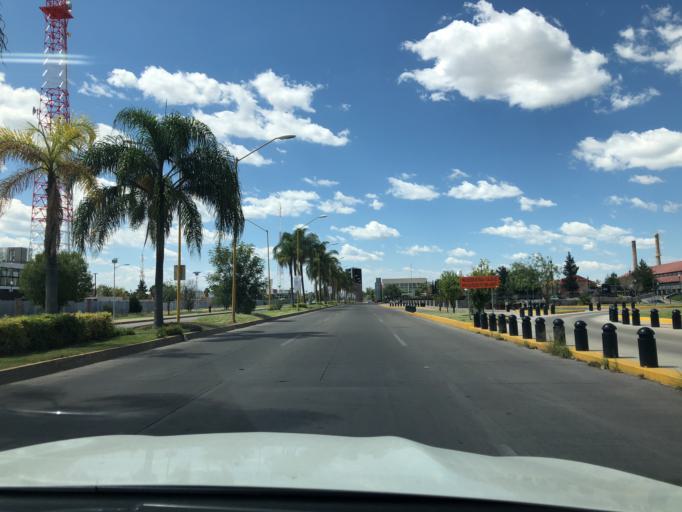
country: MX
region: Aguascalientes
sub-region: Aguascalientes
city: Aguascalientes
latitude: 21.8844
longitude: -102.2795
